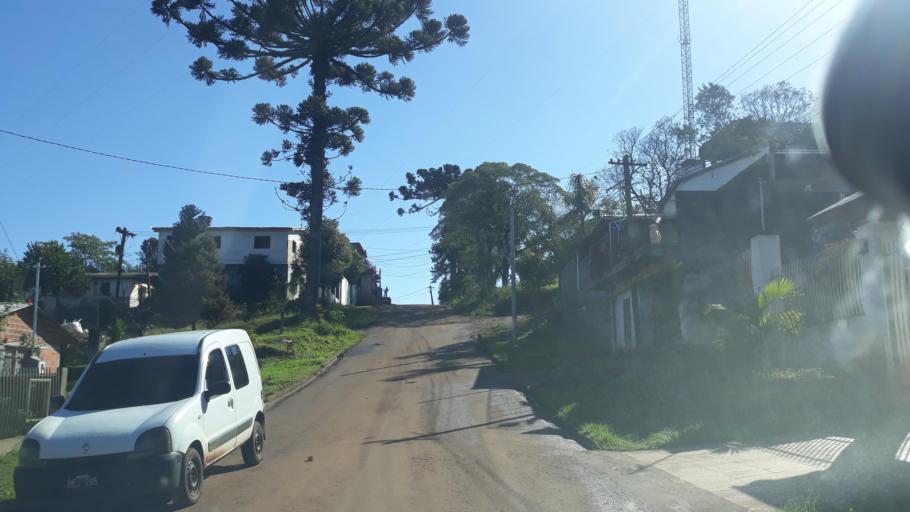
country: AR
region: Misiones
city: Bernardo de Irigoyen
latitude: -26.2598
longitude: -53.6457
